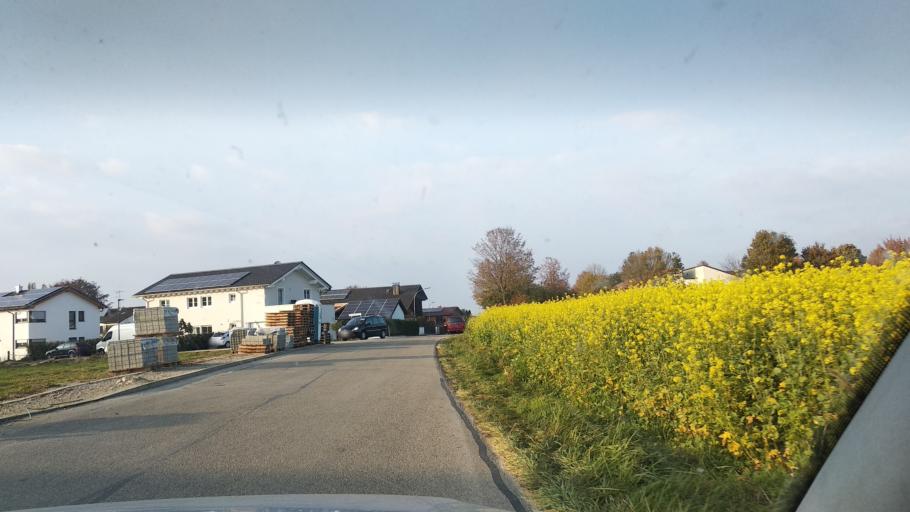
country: DE
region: Bavaria
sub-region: Upper Bavaria
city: Worth
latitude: 48.2417
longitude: 11.9022
